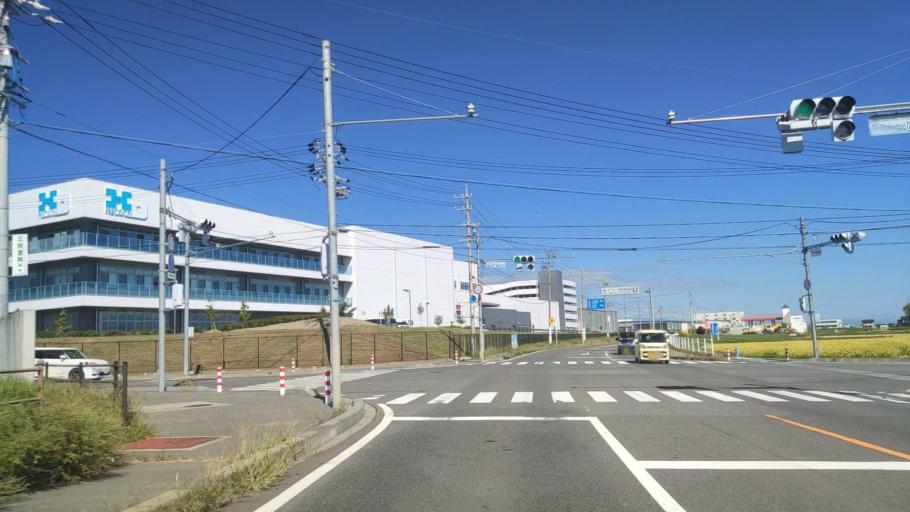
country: JP
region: Nagano
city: Matsumoto
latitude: 36.1867
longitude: 137.9036
